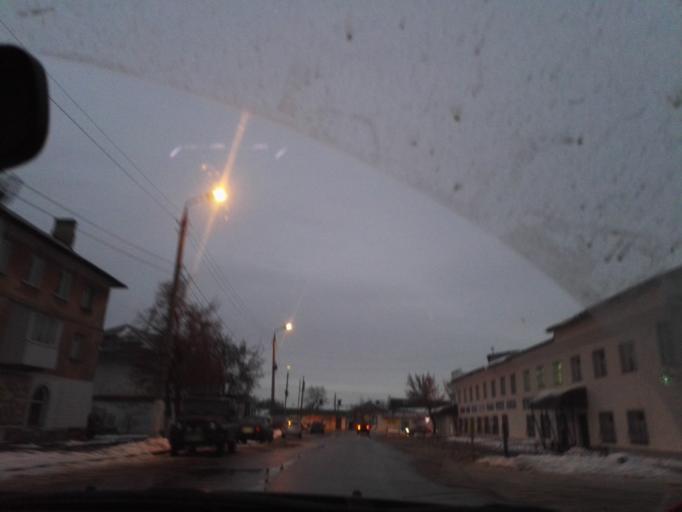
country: RU
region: Tula
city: Novomoskovsk
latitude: 54.0056
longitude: 38.3003
